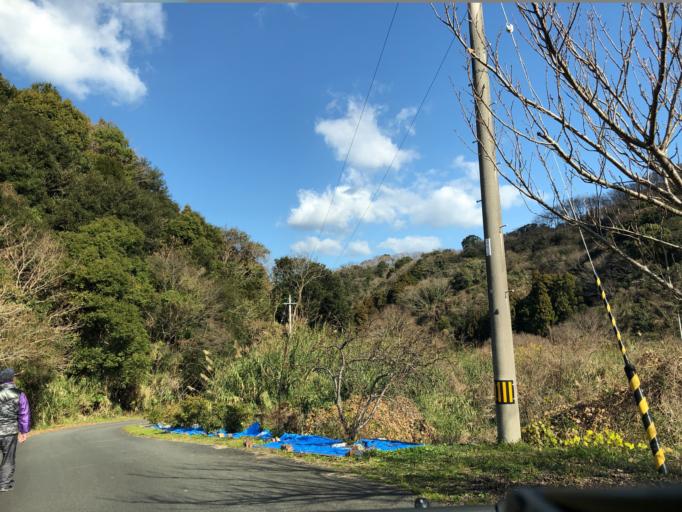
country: JP
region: Kochi
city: Sukumo
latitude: 32.9113
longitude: 132.6973
